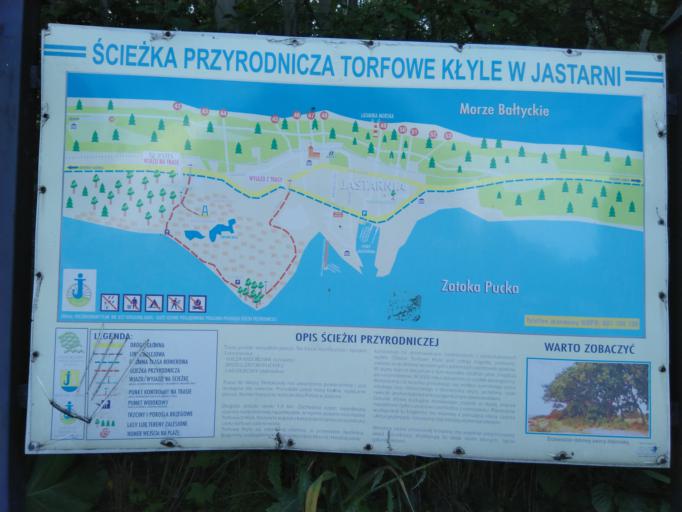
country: PL
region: Pomeranian Voivodeship
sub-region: Powiat pucki
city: Jastarnia
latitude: 54.7071
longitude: 18.6511
